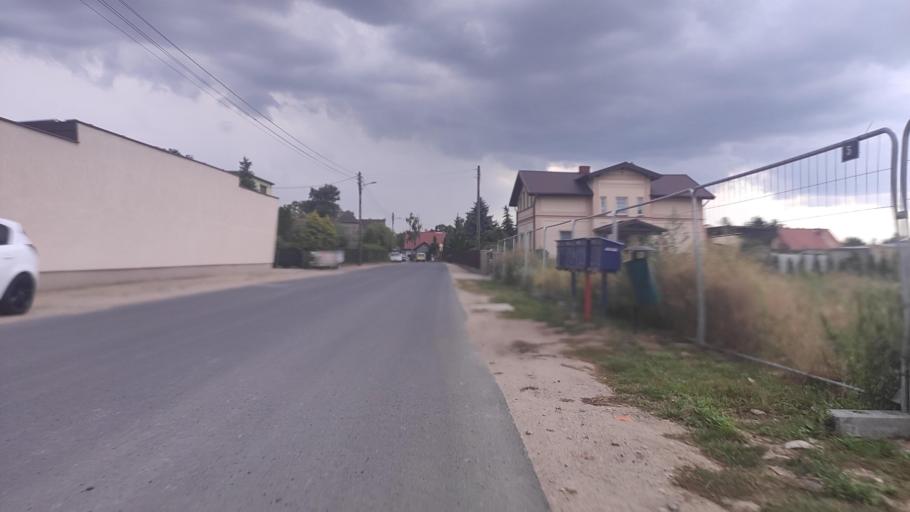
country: PL
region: Greater Poland Voivodeship
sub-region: Powiat poznanski
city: Swarzedz
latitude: 52.3879
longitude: 17.1170
